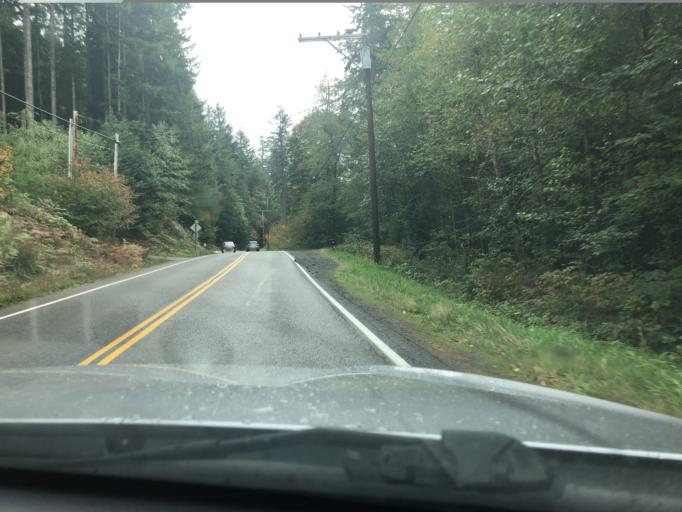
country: US
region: Washington
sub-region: King County
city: Riverbend
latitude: 47.4522
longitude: -121.7599
